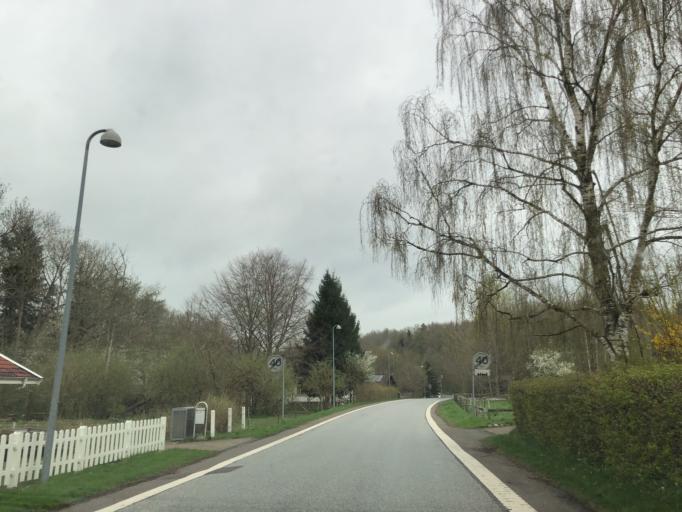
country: DK
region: Zealand
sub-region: Lejre Kommune
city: Kirke Hvalso
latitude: 55.5241
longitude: 11.8608
